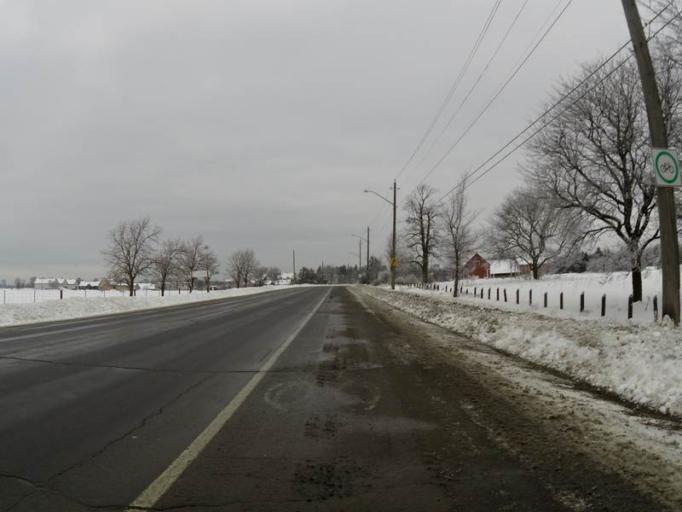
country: CA
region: Ontario
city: Ottawa
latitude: 45.3834
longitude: -75.7058
